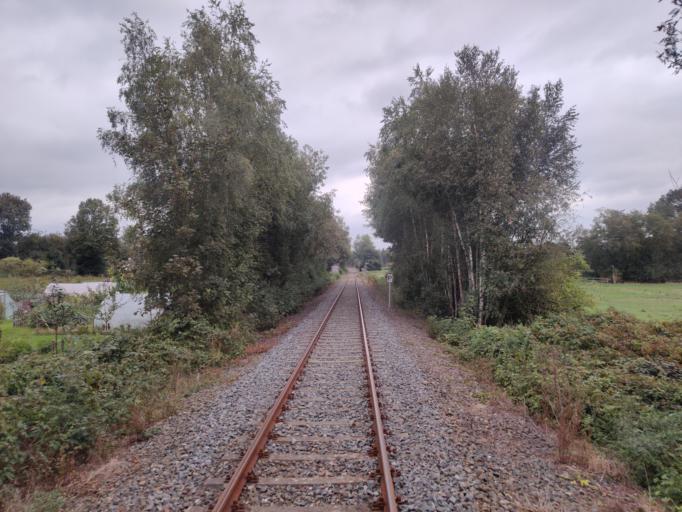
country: DE
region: Lower Saxony
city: Gnarrenburg
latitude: 53.3873
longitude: 9.0121
